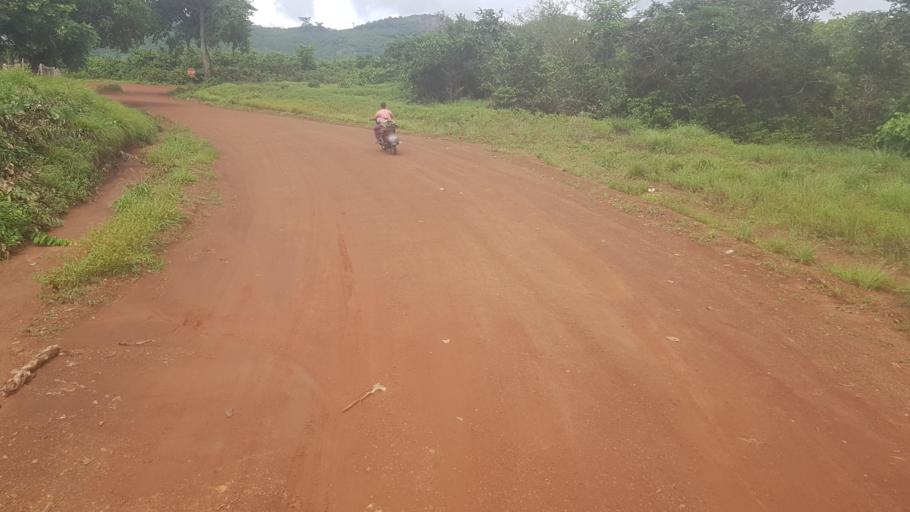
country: SL
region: Southern Province
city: Mogbwemo
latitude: 7.7529
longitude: -12.3084
